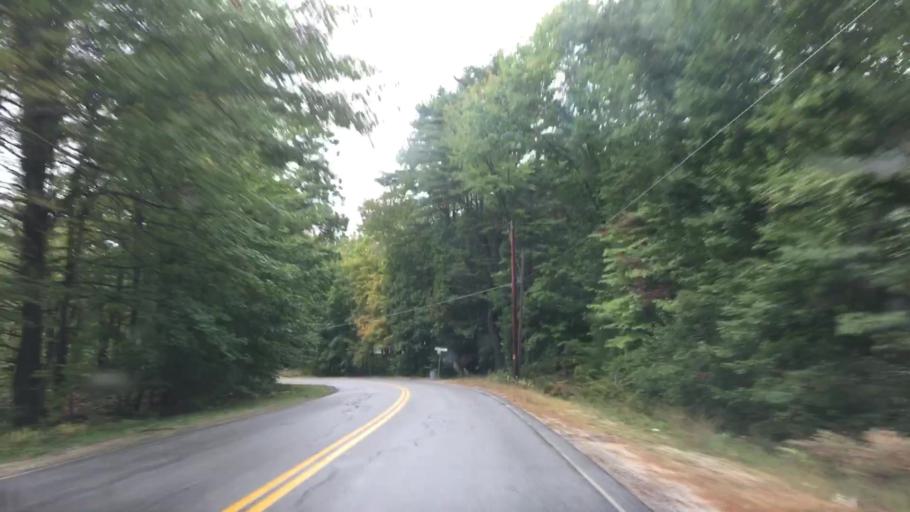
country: US
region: Maine
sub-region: Cumberland County
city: Raymond
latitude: 43.9387
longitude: -70.4276
